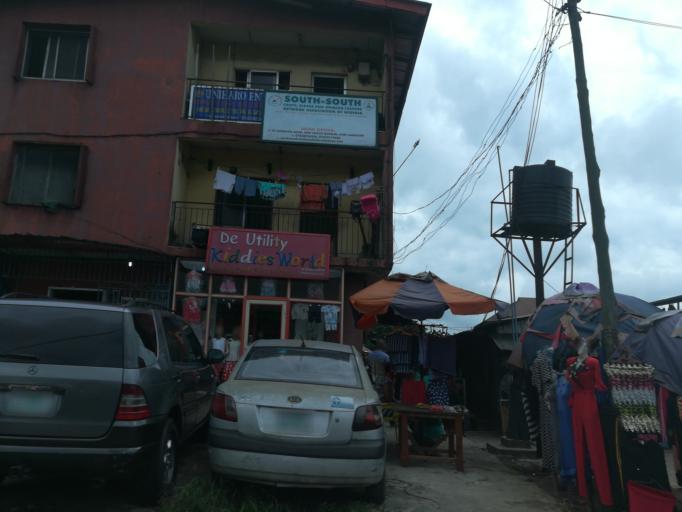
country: NG
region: Rivers
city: Port Harcourt
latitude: 4.7571
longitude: 7.0362
